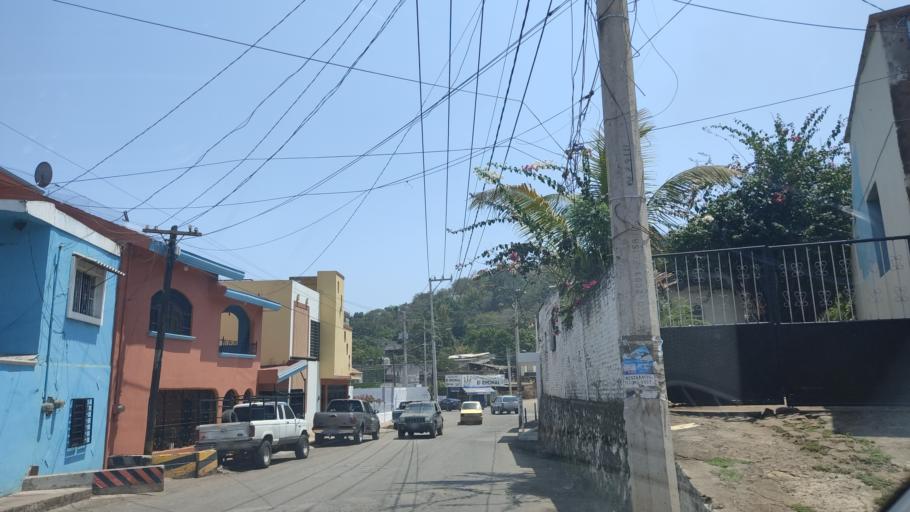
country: MX
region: Nayarit
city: Puga
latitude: 21.5836
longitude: -104.8207
